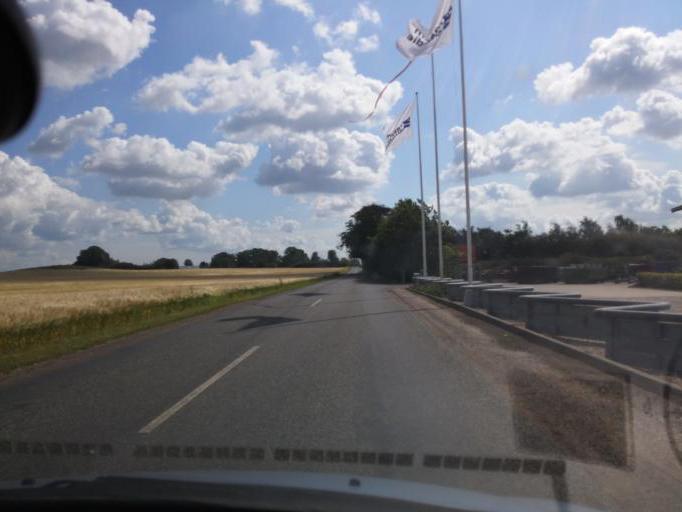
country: DK
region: South Denmark
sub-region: Odense Kommune
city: Bullerup
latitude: 55.3964
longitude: 10.4873
